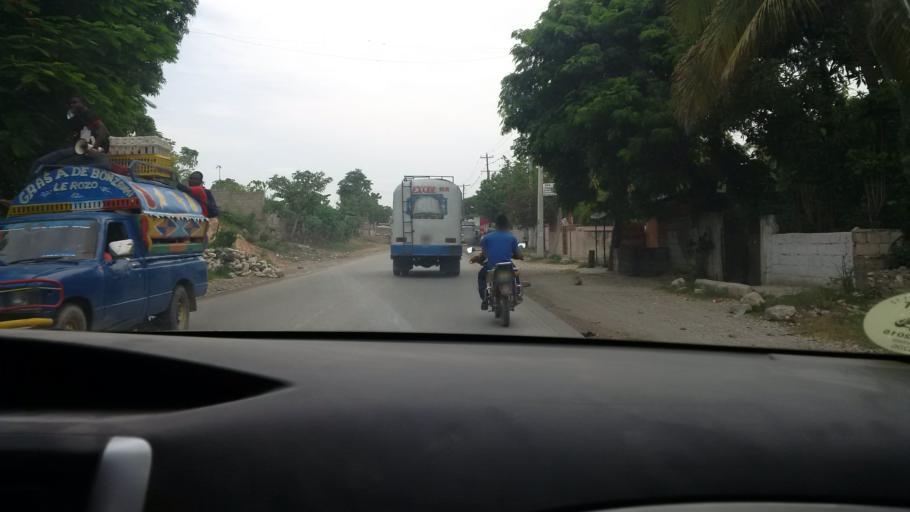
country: HT
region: Ouest
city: Gressier
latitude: 18.5429
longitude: -72.5213
